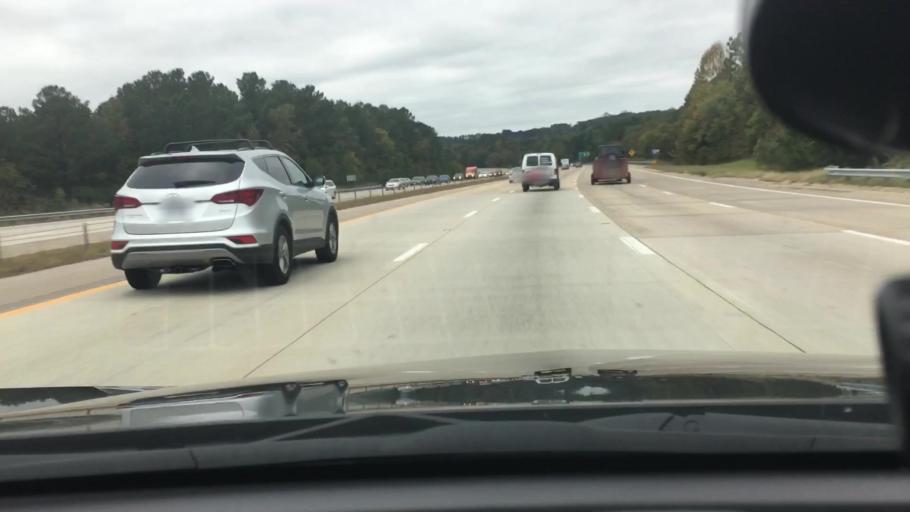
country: US
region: North Carolina
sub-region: Wake County
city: Knightdale
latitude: 35.7700
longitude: -78.5288
